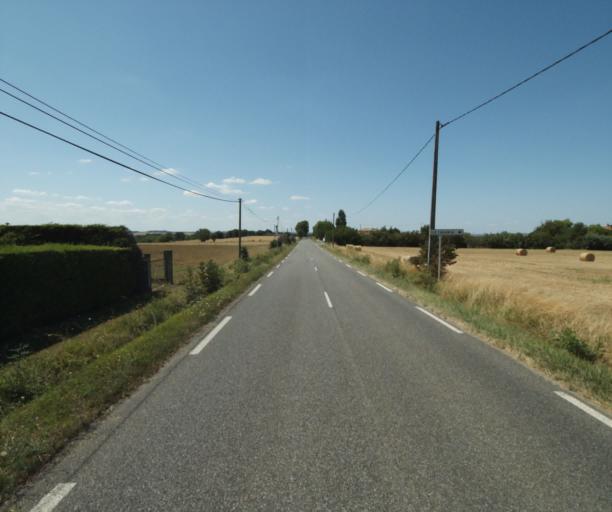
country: FR
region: Midi-Pyrenees
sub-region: Departement de la Haute-Garonne
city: Saint-Felix-Lauragais
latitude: 43.5007
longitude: 1.8809
